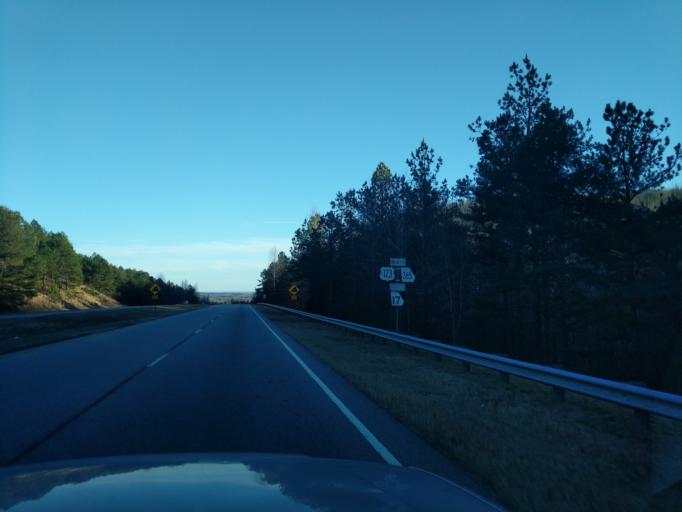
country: US
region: Georgia
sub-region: Stephens County
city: Toccoa
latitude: 34.5586
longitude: -83.3879
